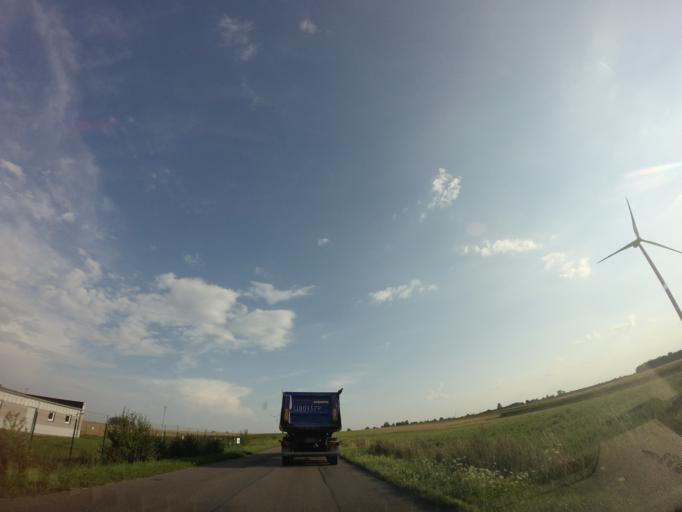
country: PL
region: Lublin Voivodeship
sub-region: Powiat lubartowski
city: Michow
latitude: 51.5023
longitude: 22.3072
